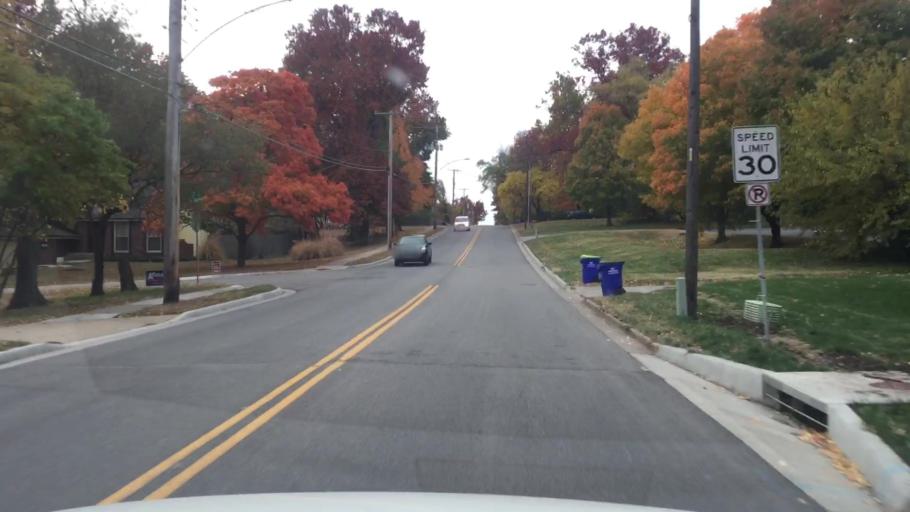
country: US
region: Kansas
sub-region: Johnson County
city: Shawnee
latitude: 39.0327
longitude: -94.7240
